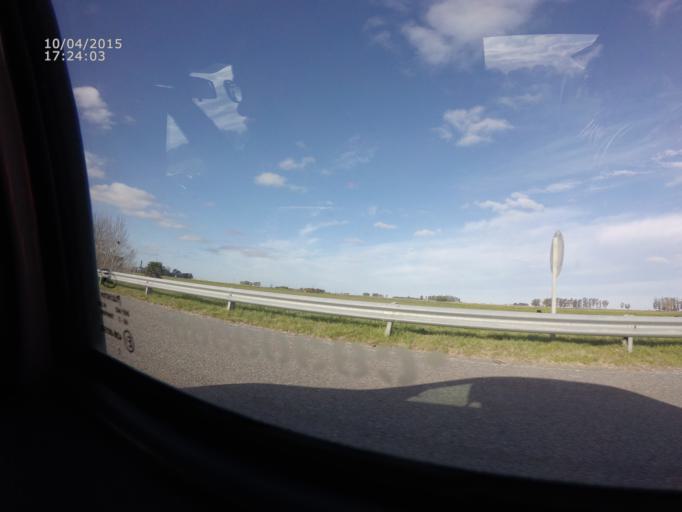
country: AR
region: Buenos Aires
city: Maipu
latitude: -37.0905
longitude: -57.8272
